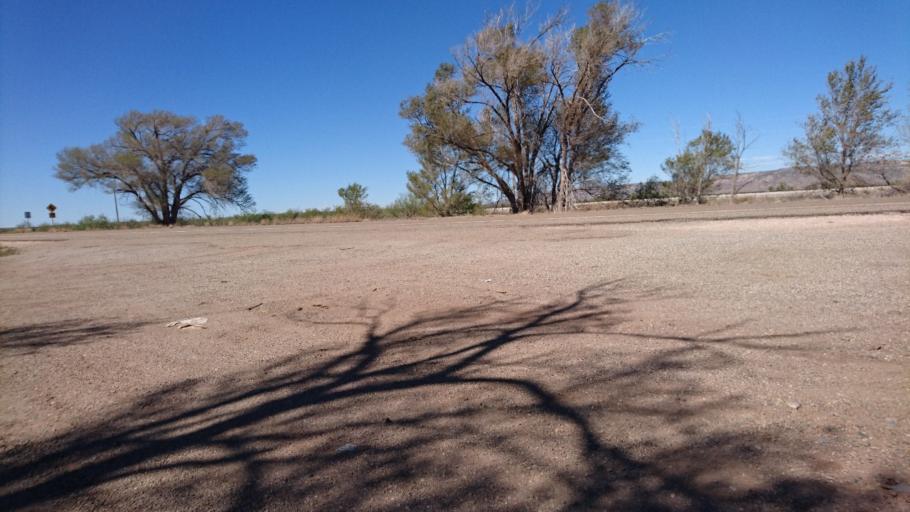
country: US
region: New Mexico
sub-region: Quay County
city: Tucumcari
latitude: 35.0955
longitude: -104.0658
